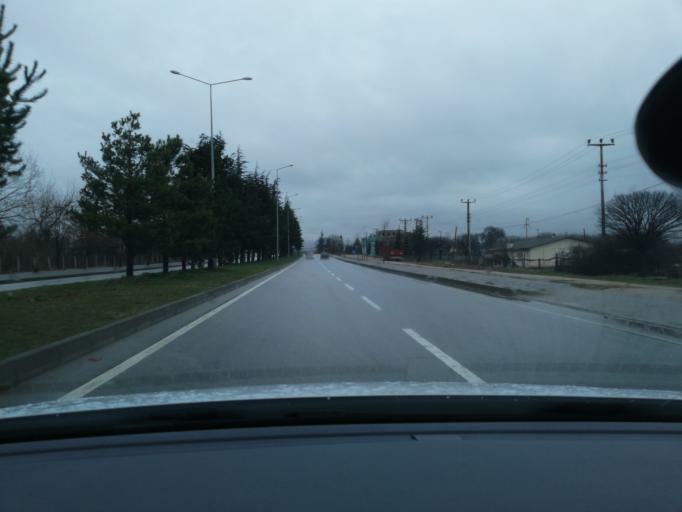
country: TR
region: Bolu
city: Bolu
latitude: 40.7095
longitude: 31.6165
